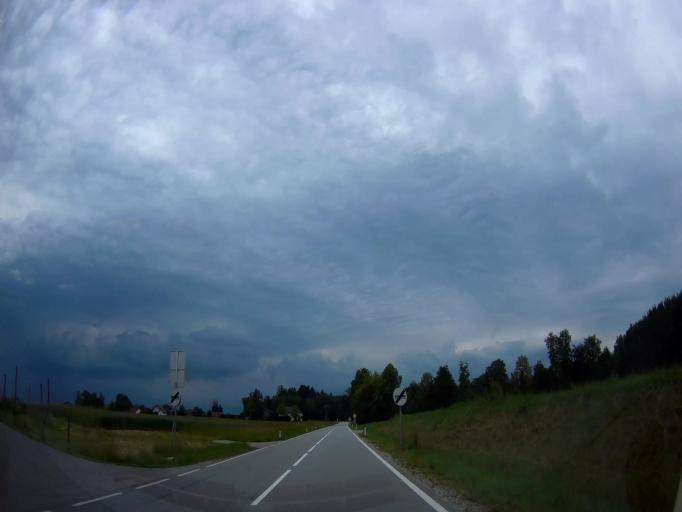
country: AT
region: Upper Austria
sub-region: Politischer Bezirk Braunau am Inn
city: Altheim
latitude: 48.1956
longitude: 13.1480
